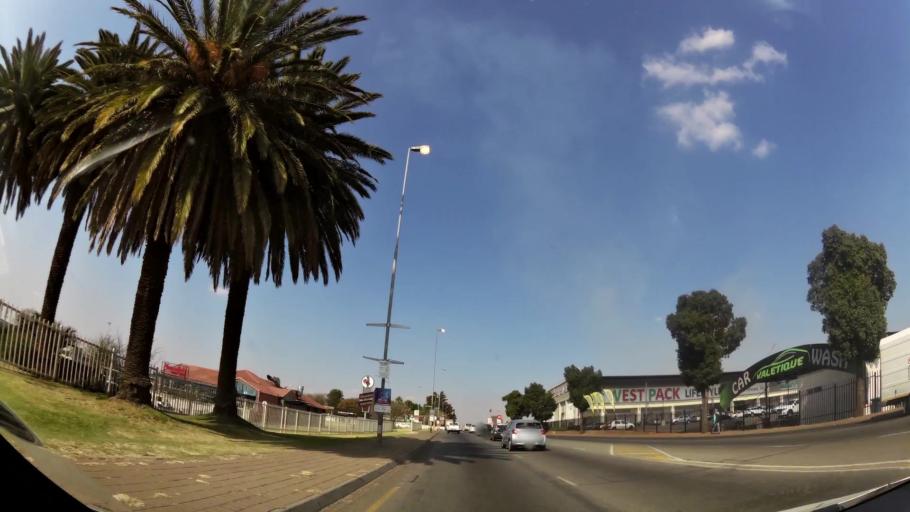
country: ZA
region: Gauteng
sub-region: Ekurhuleni Metropolitan Municipality
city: Boksburg
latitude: -26.1821
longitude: 28.2364
